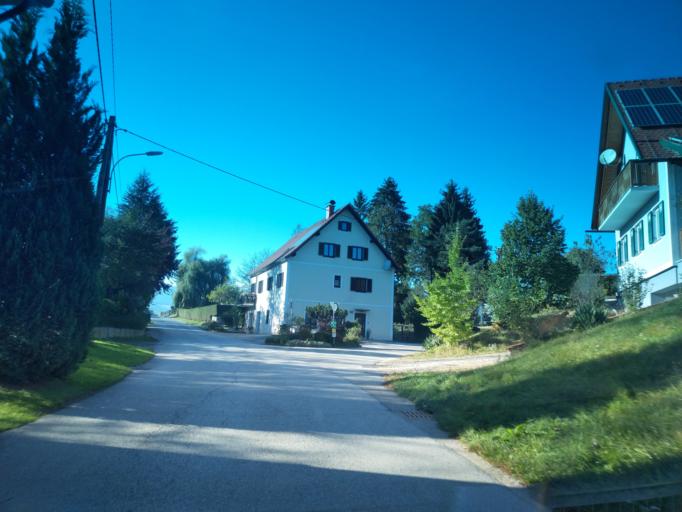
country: AT
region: Styria
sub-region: Politischer Bezirk Deutschlandsberg
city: Stallhof
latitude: 46.8884
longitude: 15.2972
